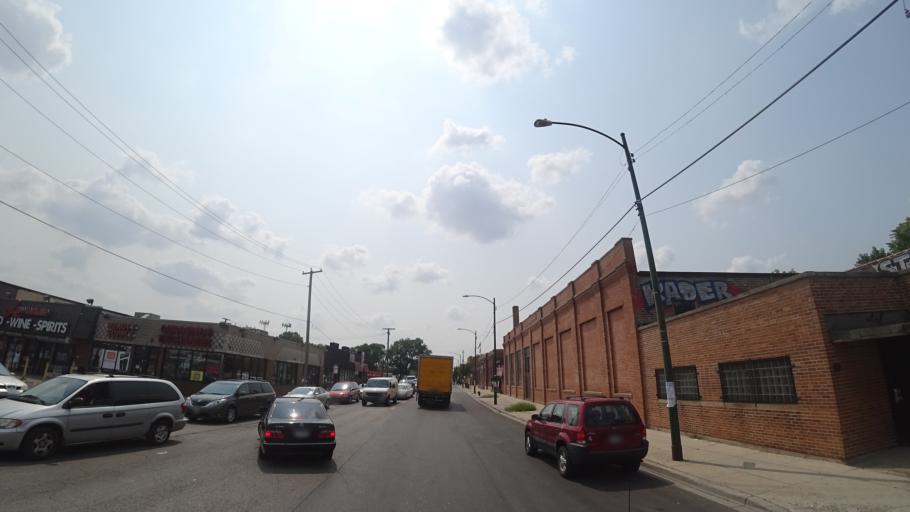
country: US
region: Illinois
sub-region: Cook County
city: Cicero
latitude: 41.8506
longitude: -87.7248
